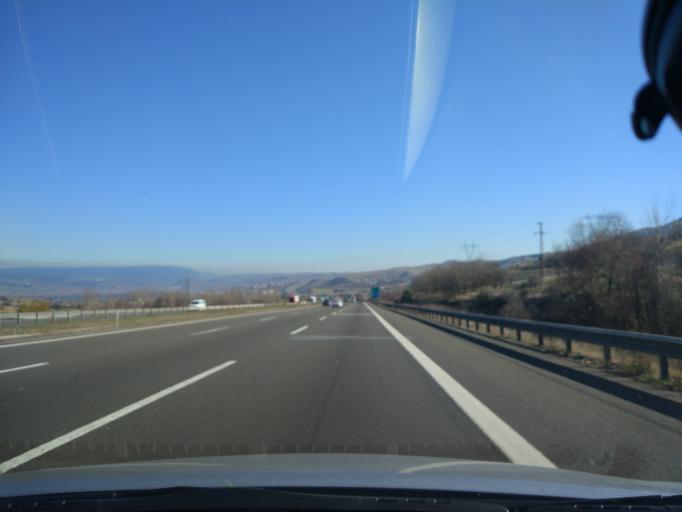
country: TR
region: Bolu
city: Yenicaga
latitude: 40.7618
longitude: 31.9884
